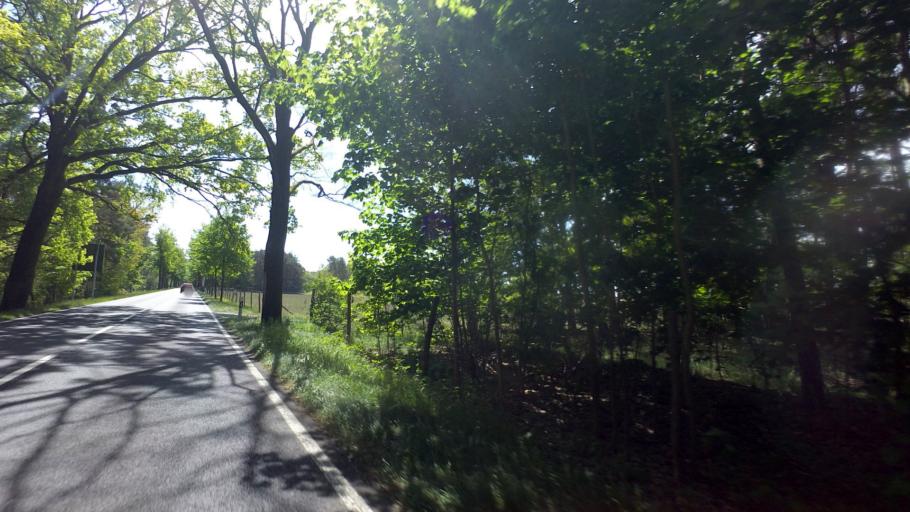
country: DE
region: Brandenburg
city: Luckenwalde
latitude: 52.1220
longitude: 13.1338
